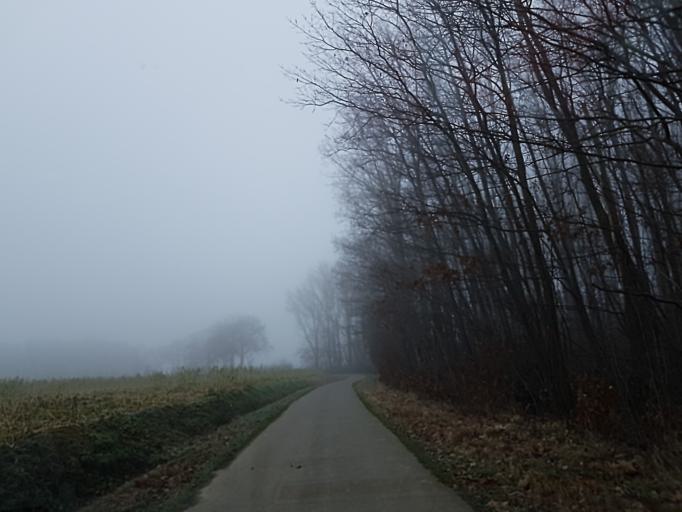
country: BE
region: Flanders
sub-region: Provincie Vlaams-Brabant
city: Zemst
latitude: 50.9836
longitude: 4.4368
